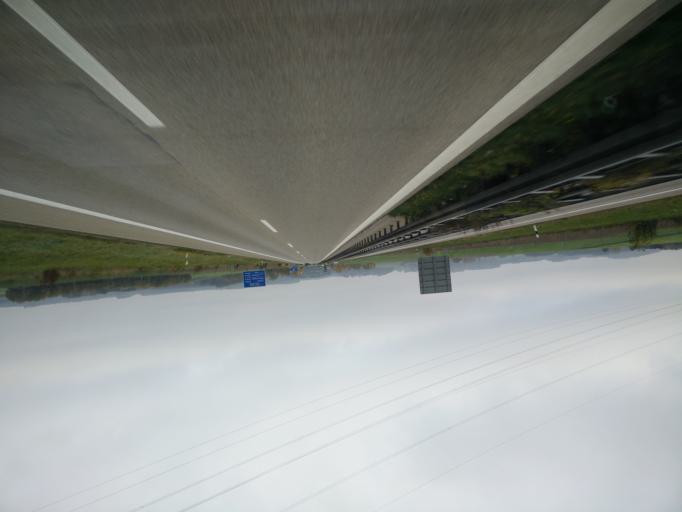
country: DE
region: Bavaria
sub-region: Swabia
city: Stetten
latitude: 48.0331
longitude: 10.4347
